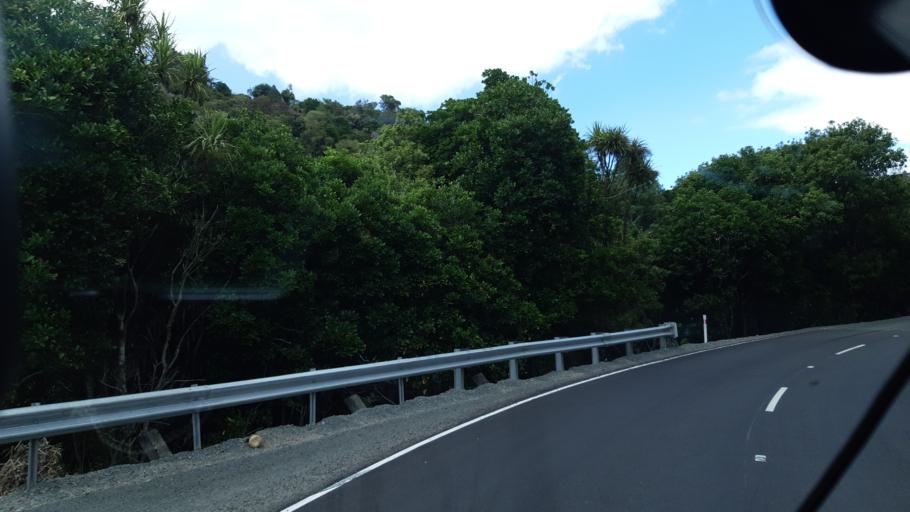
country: NZ
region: Northland
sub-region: Far North District
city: Taipa
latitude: -35.2464
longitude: 173.5353
